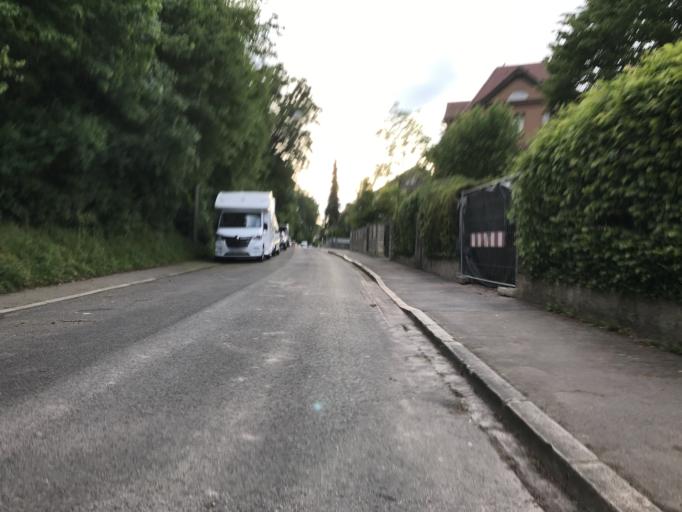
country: DE
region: Baden-Wuerttemberg
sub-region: Regierungsbezirk Stuttgart
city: Stuttgart Feuerbach
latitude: 48.8286
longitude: 9.1634
